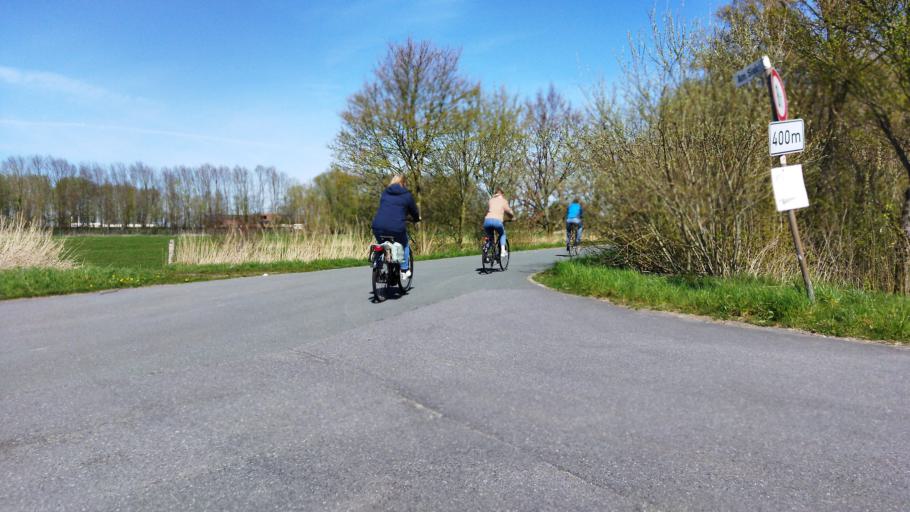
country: DE
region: Lower Saxony
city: Brake (Unterweser)
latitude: 53.3565
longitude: 8.4825
